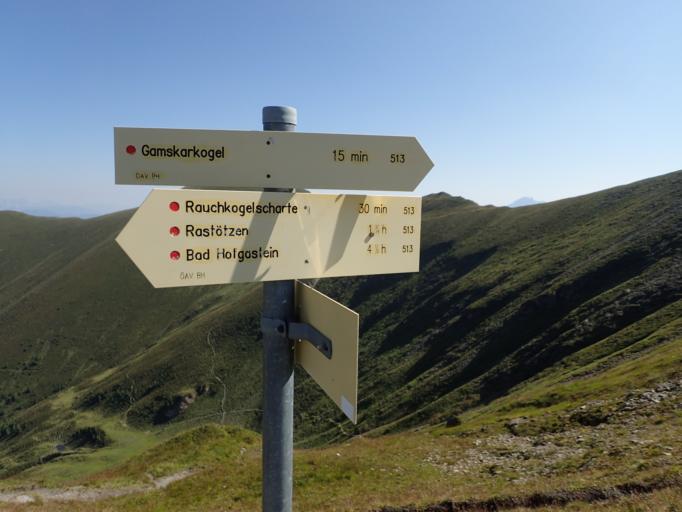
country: AT
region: Salzburg
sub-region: Politischer Bezirk Sankt Johann im Pongau
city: Bad Gastein
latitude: 47.1633
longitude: 13.1551
